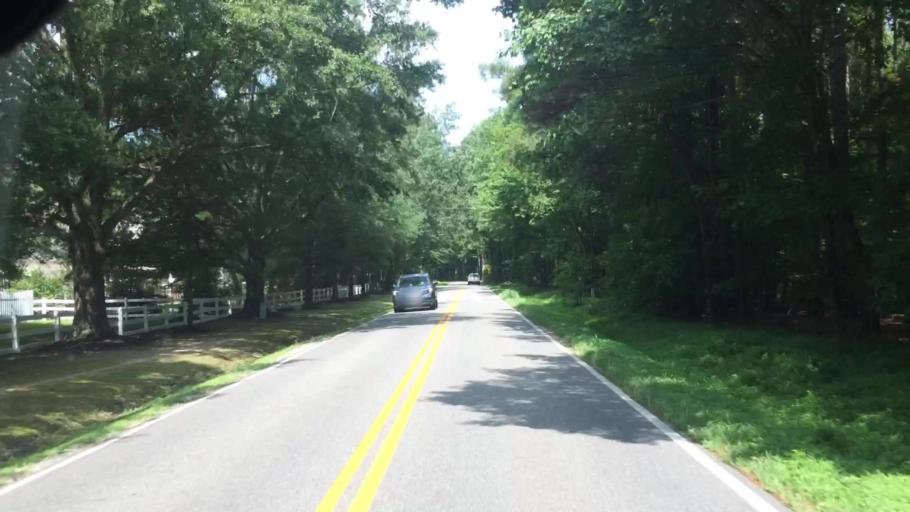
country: US
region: Virginia
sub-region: James City County
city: Williamsburg
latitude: 37.2381
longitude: -76.7871
